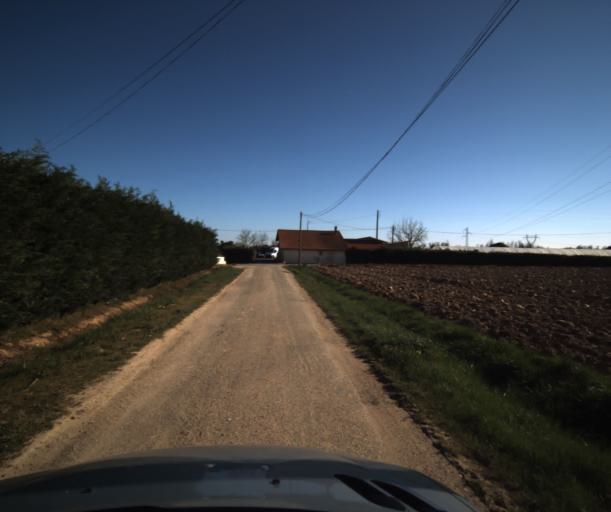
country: FR
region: Midi-Pyrenees
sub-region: Departement du Tarn-et-Garonne
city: Bressols
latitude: 43.9407
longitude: 1.3310
